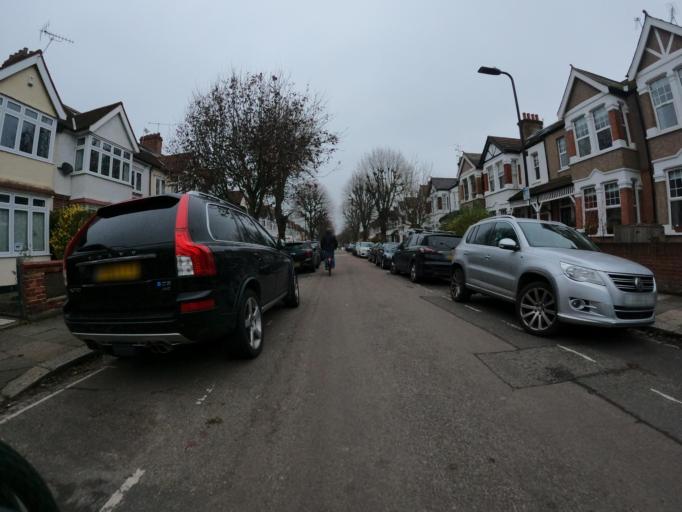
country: GB
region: England
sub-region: Greater London
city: Brentford
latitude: 51.4952
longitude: -0.3120
